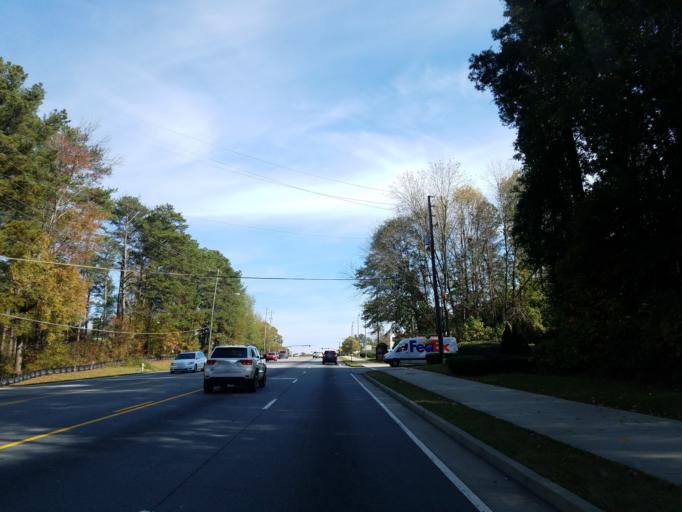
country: US
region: Georgia
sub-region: Cobb County
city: Marietta
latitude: 33.9326
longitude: -84.5614
